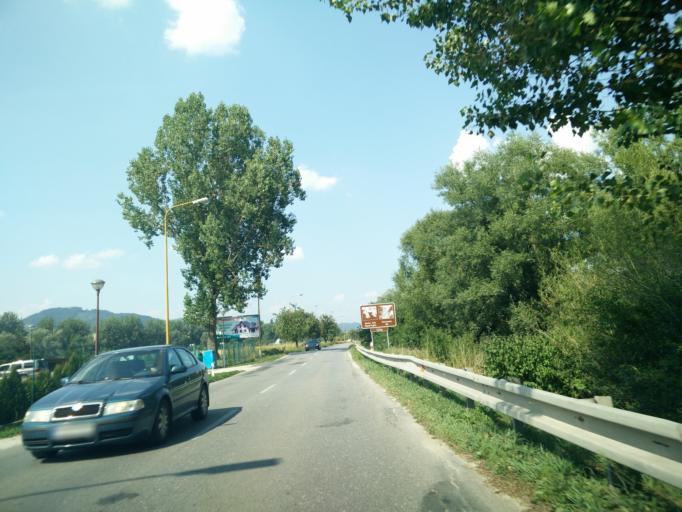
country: SK
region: Zilinsky
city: Rajec
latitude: 49.0733
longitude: 18.6297
